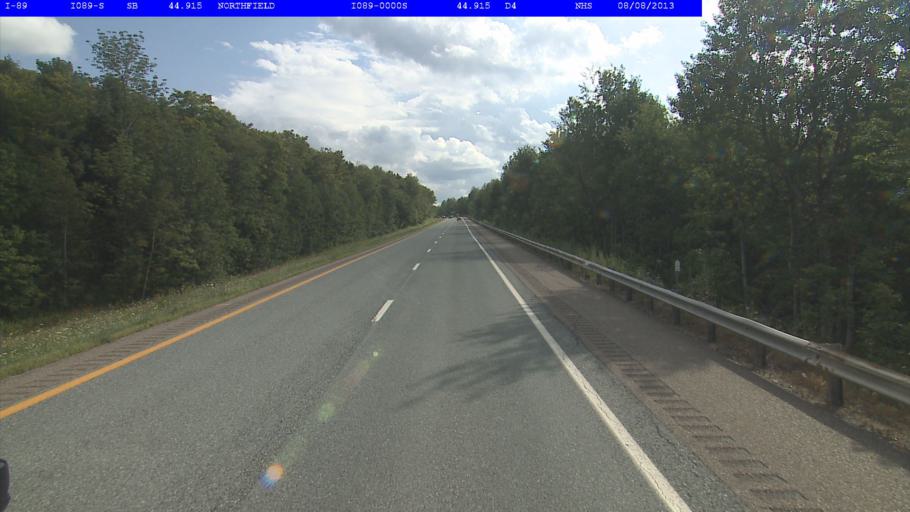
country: US
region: Vermont
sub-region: Orange County
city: Williamstown
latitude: 44.1423
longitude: -72.5973
